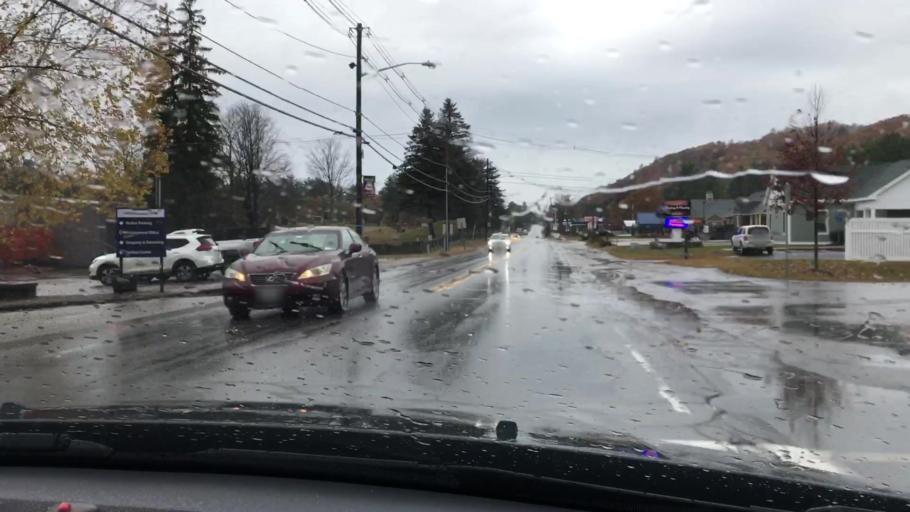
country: US
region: New Hampshire
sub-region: Grafton County
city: Ashland
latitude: 43.6969
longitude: -71.6385
